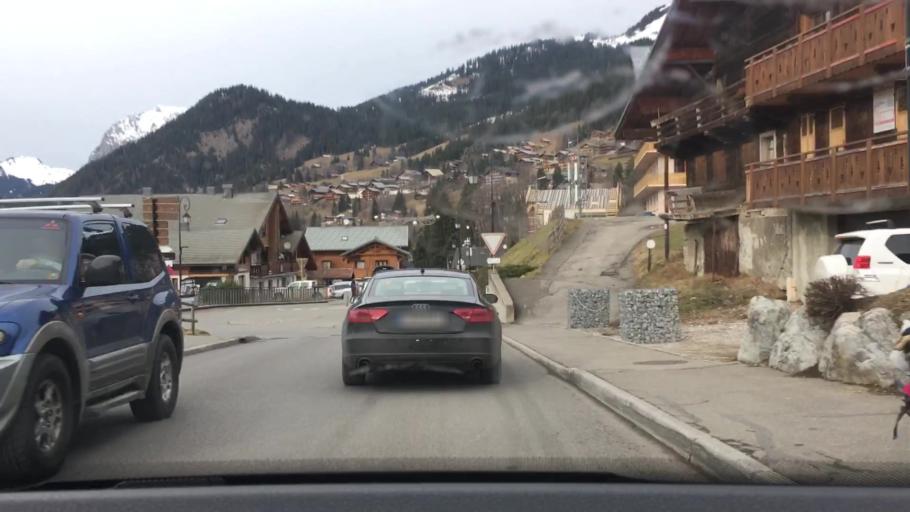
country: FR
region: Rhone-Alpes
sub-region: Departement de la Haute-Savoie
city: Chatel
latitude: 46.2689
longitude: 6.8407
